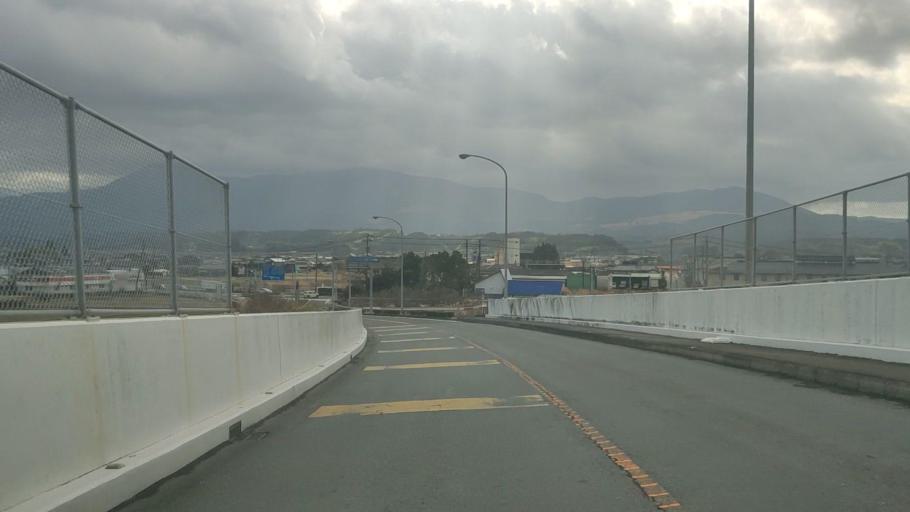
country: JP
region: Kumamoto
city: Hitoyoshi
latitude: 32.0543
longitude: 130.8170
